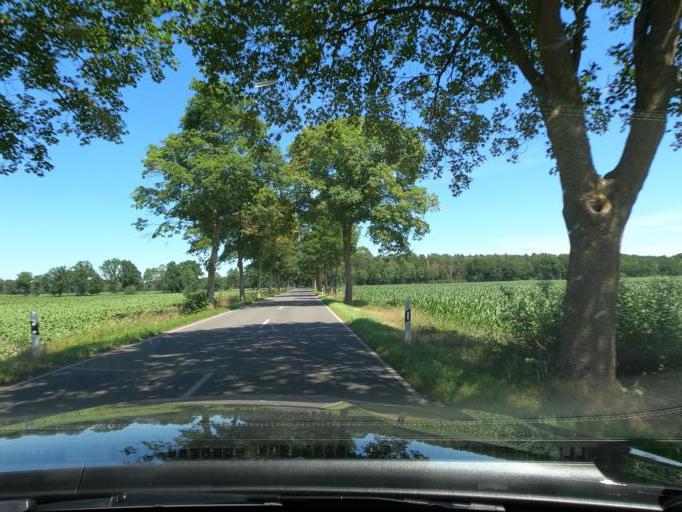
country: DE
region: Lower Saxony
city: Haenigsen
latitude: 52.4959
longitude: 10.1216
